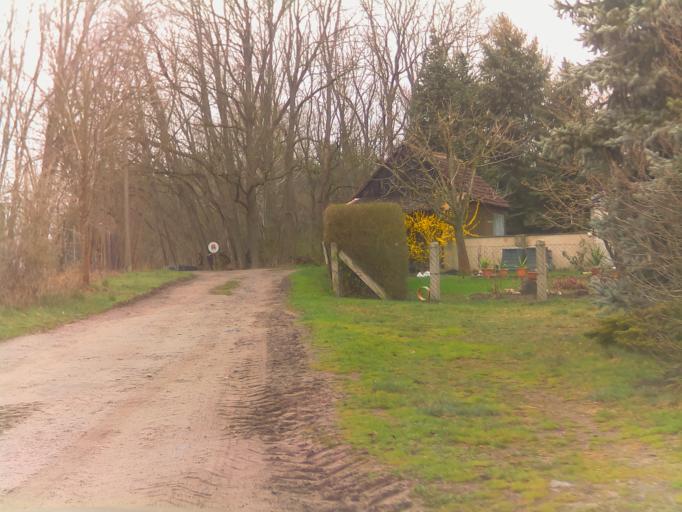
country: DE
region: Brandenburg
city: Neu Zauche
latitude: 51.9628
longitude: 14.1324
